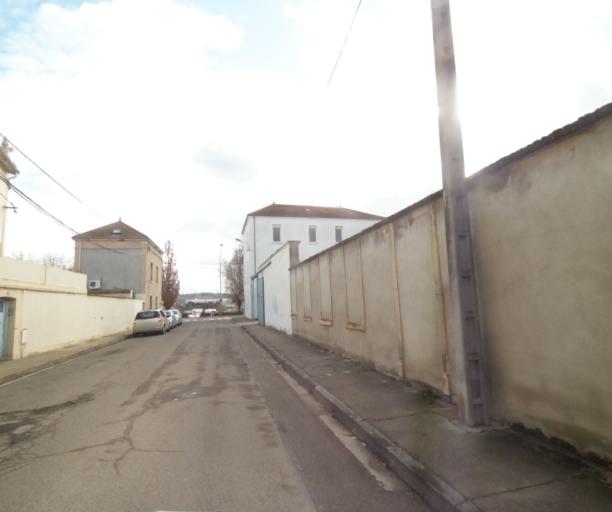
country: FR
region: Rhone-Alpes
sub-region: Departement de la Loire
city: Le Coteau
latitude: 46.0361
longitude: 4.0790
